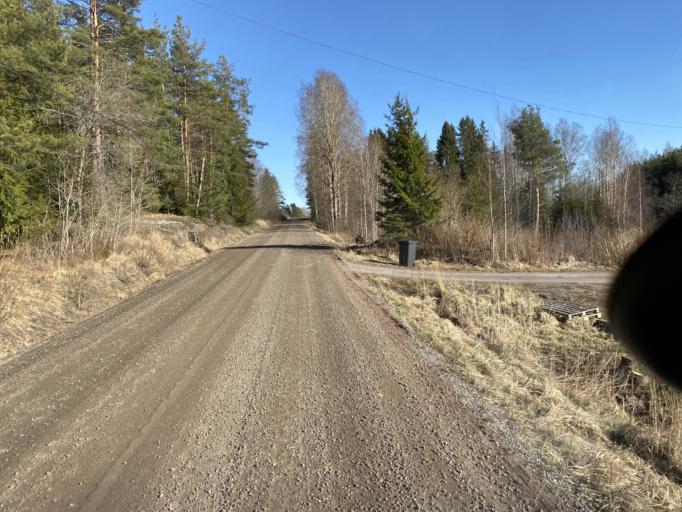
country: FI
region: Satakunta
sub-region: Rauma
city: Lappi
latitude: 61.1421
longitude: 21.9323
